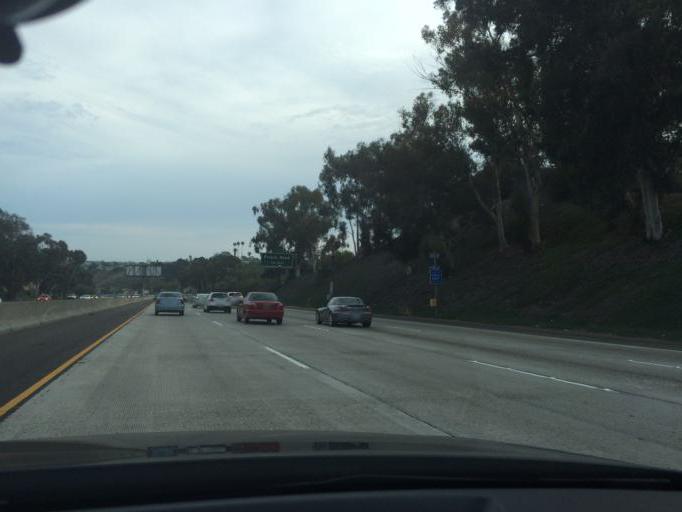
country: US
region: California
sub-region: San Diego County
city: San Diego
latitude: 32.7848
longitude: -117.1616
